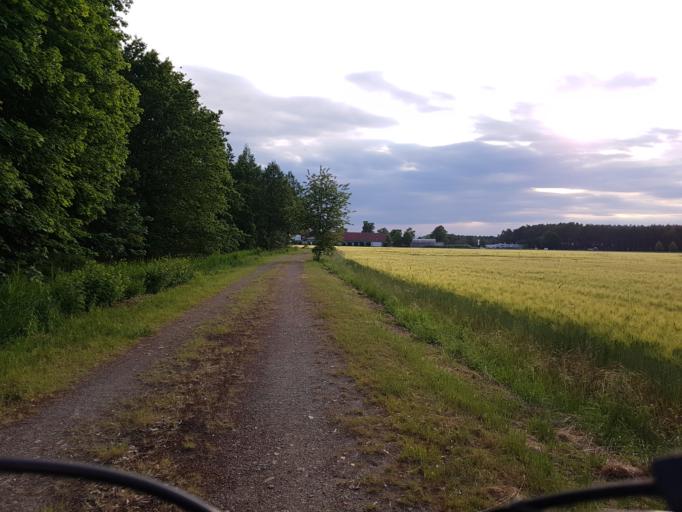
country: DE
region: Brandenburg
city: Bad Liebenwerda
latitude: 51.5302
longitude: 13.4029
